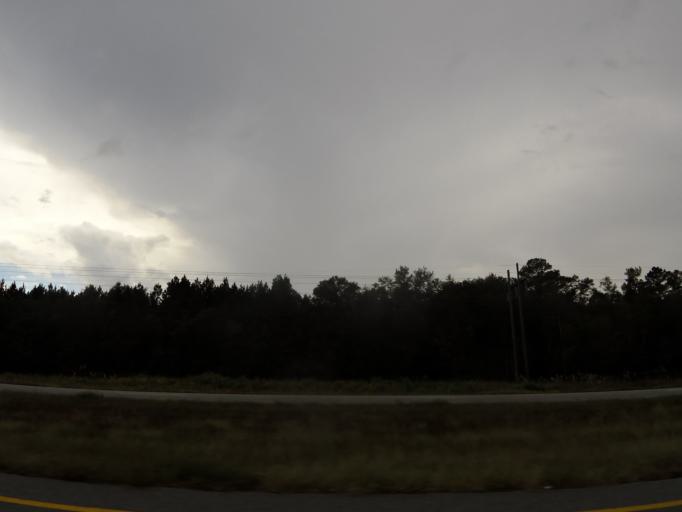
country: US
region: Georgia
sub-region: McIntosh County
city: Darien
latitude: 31.4029
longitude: -81.6519
